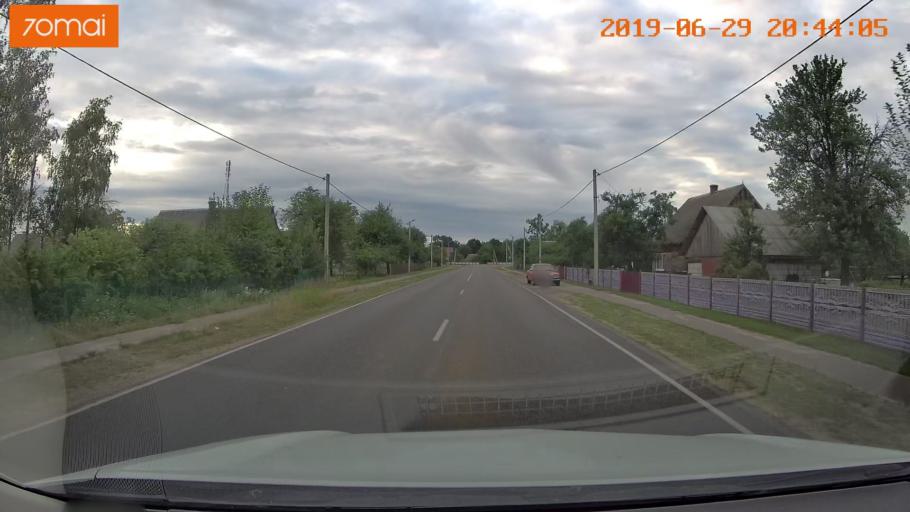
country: BY
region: Brest
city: Hantsavichy
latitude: 52.6104
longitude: 26.3090
